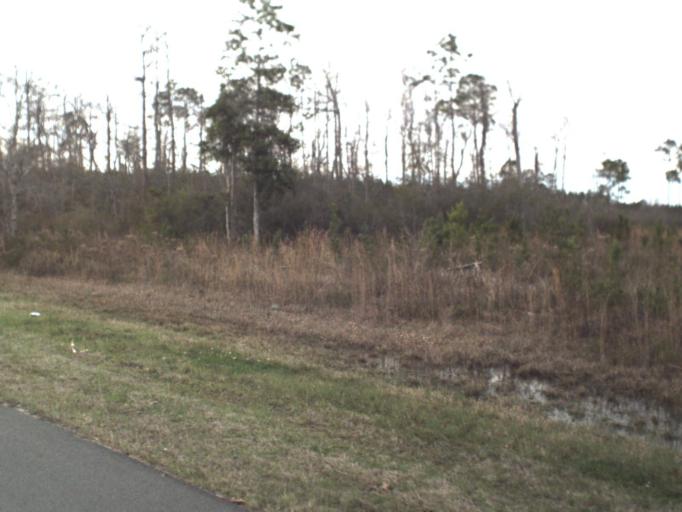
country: US
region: Florida
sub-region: Gulf County
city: Wewahitchka
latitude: 30.1391
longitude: -85.2524
